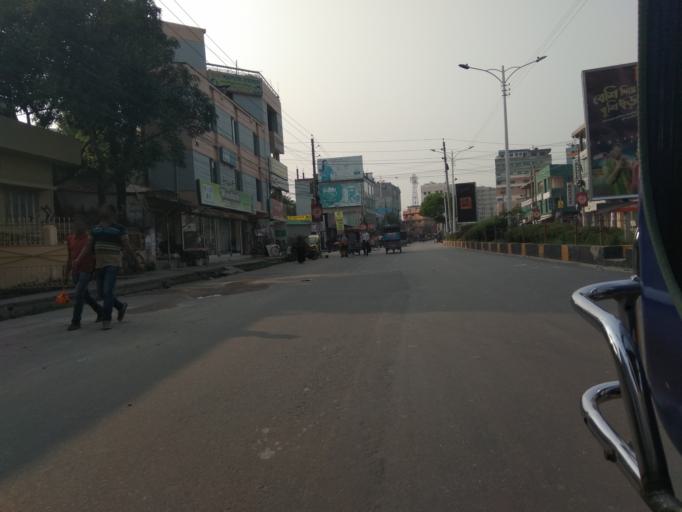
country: BD
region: Khulna
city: Khulna
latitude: 22.8139
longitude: 89.5557
